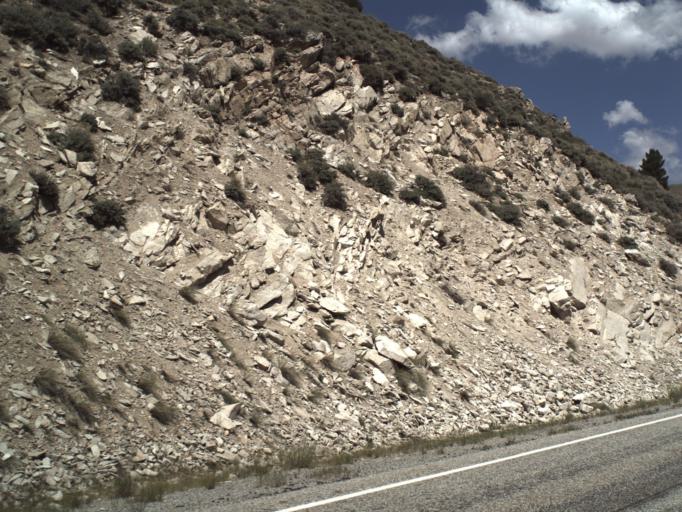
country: US
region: Utah
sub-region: Rich County
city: Randolph
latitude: 41.4843
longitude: -111.4014
